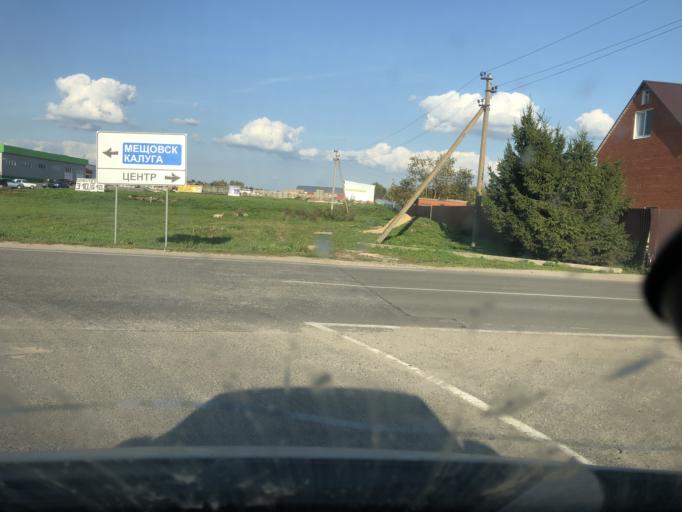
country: RU
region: Kaluga
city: Kozel'sk
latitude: 54.0556
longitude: 35.7907
